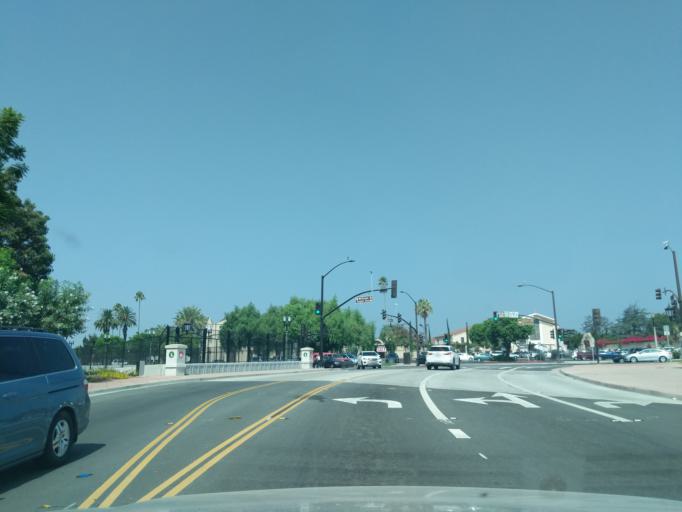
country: US
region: California
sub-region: Los Angeles County
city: San Gabriel
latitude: 34.0963
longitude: -118.1051
